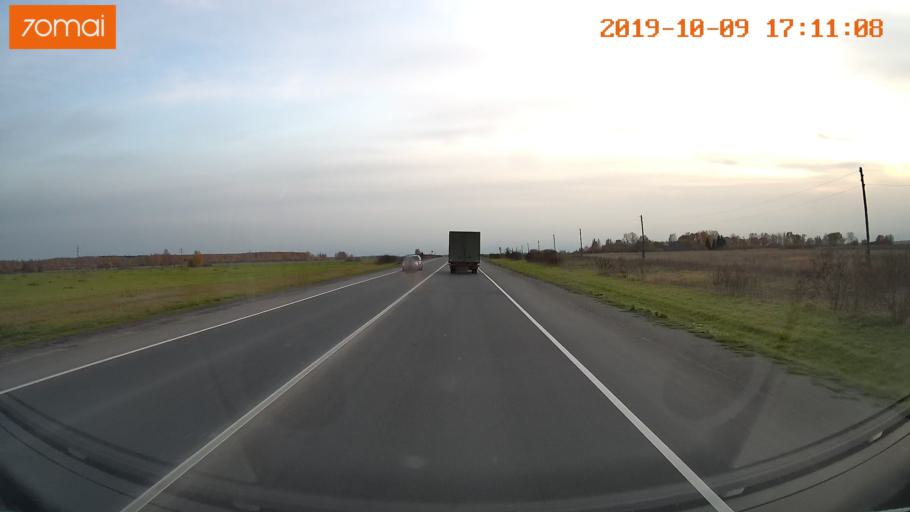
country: RU
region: Ivanovo
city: Privolzhsk
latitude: 57.3469
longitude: 41.2516
